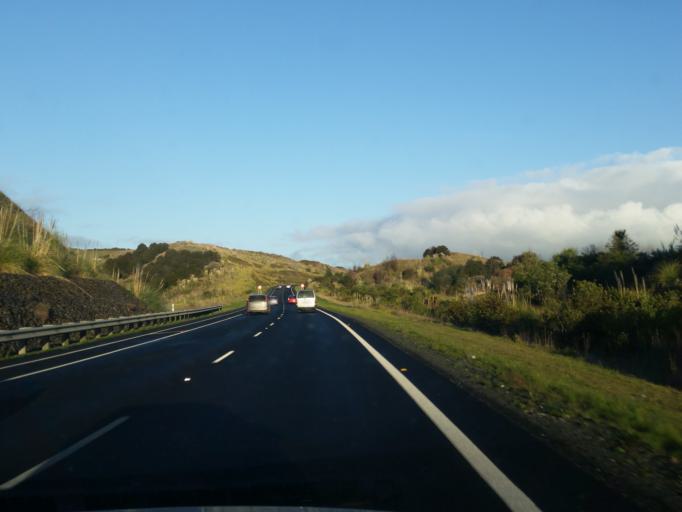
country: NZ
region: Auckland
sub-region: Auckland
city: Pukekohe East
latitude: -37.2859
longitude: 175.0533
